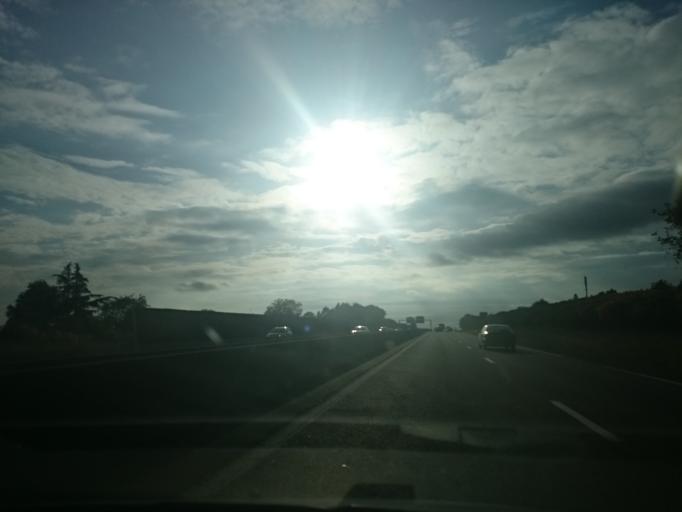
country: FR
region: Brittany
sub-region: Departement du Morbihan
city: Theix
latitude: 47.6416
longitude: -2.6861
